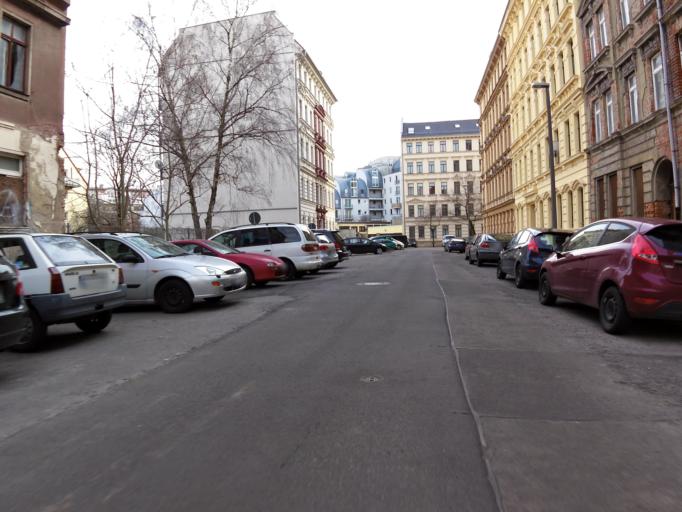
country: DE
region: Saxony
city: Leipzig
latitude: 51.3459
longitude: 12.3967
